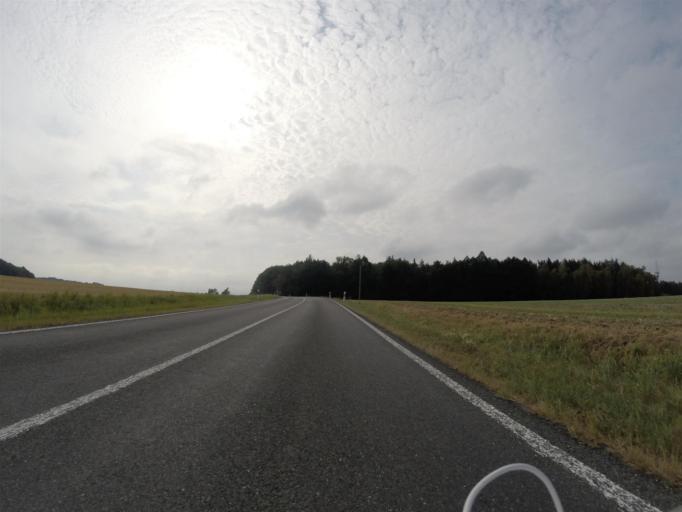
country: DE
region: Thuringia
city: Scheiditz
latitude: 50.9007
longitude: 11.7390
